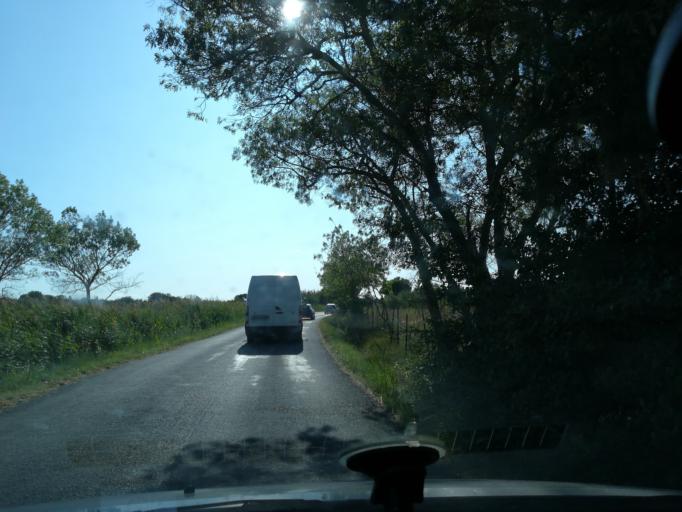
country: FR
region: Languedoc-Roussillon
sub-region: Departement de l'Herault
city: Vias
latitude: 43.2941
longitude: 3.3930
